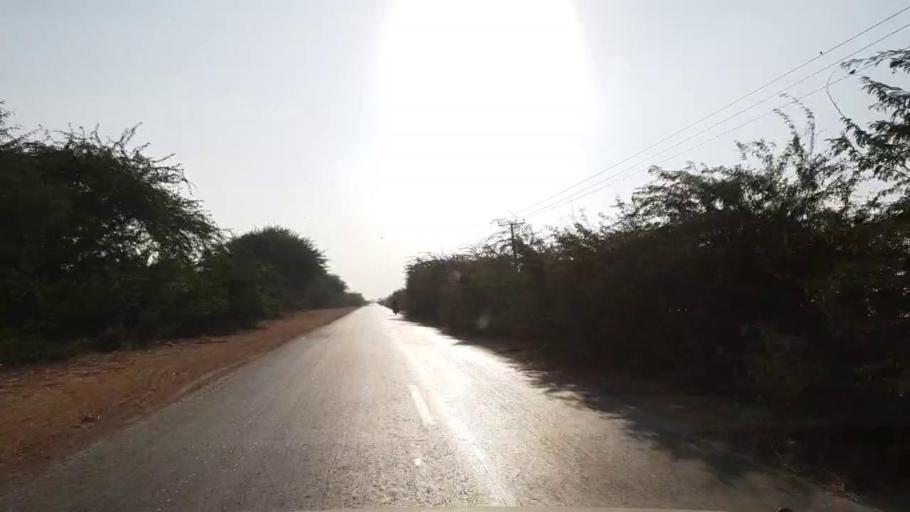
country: PK
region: Sindh
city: Bulri
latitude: 24.7989
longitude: 68.3056
